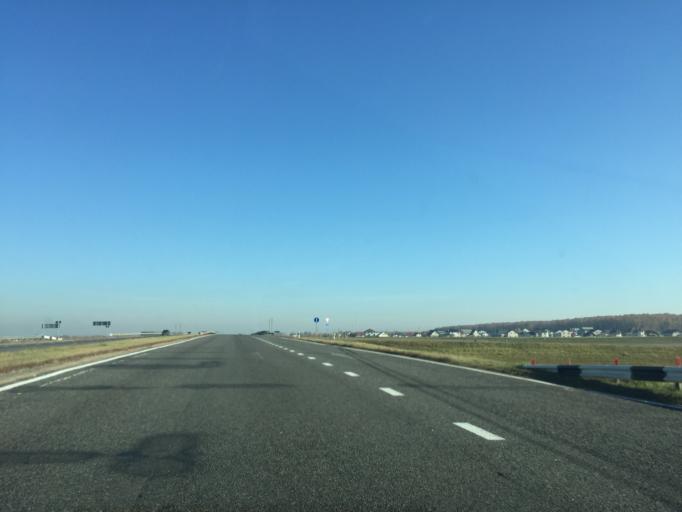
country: BY
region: Mogilev
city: Buynichy
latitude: 53.9472
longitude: 30.2208
